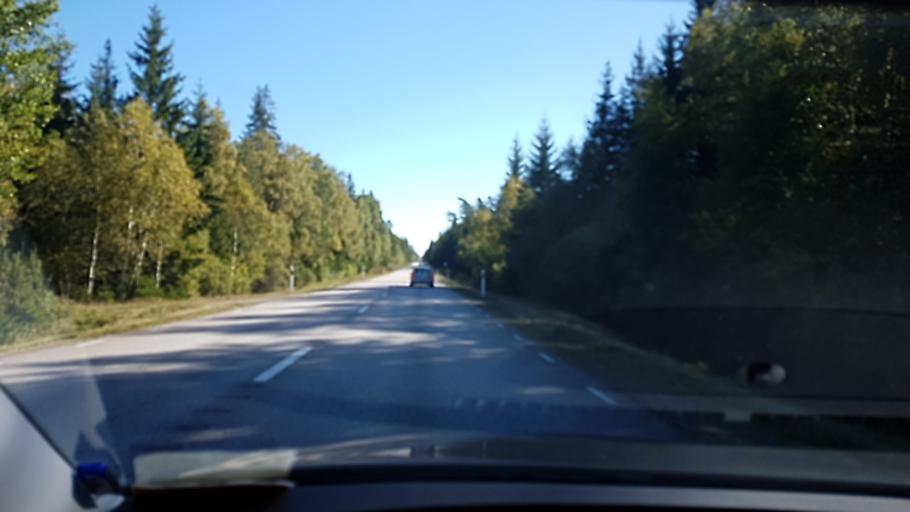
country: SE
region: Kronoberg
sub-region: Lessebo Kommun
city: Lessebo
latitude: 56.7301
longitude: 15.3726
